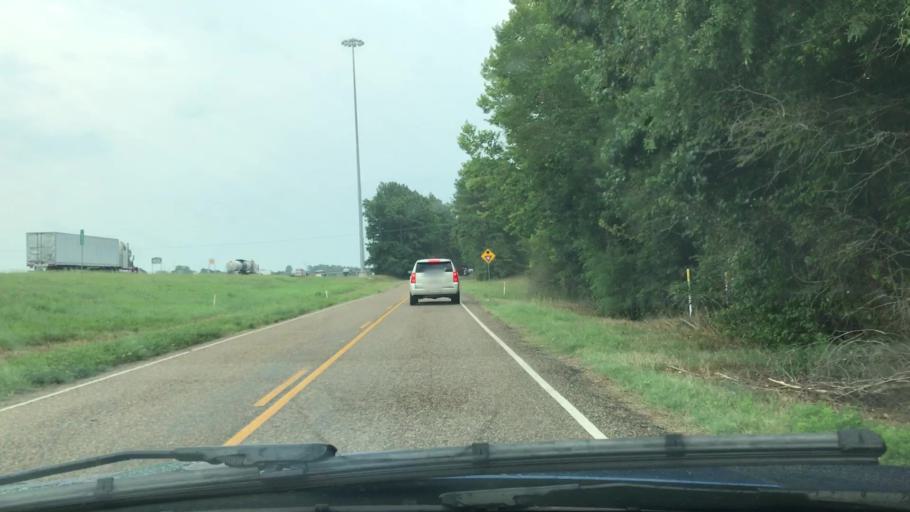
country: US
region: Texas
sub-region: Harrison County
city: Waskom
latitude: 32.4795
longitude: -94.0929
